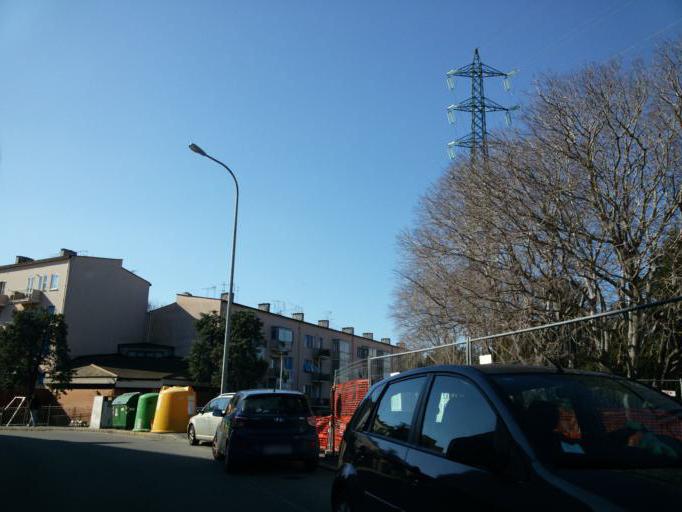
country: IT
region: Liguria
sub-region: Provincia di Genova
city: San Teodoro
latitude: 44.4142
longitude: 8.9043
